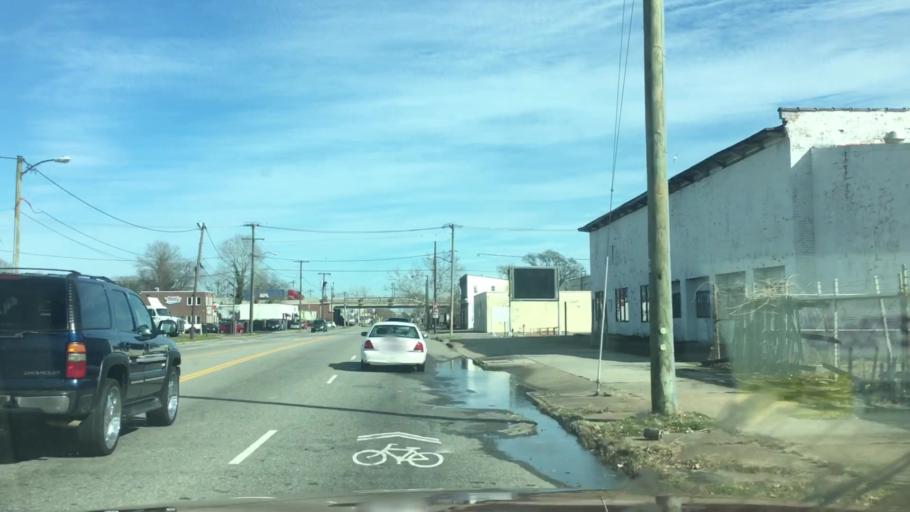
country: US
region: Virginia
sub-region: City of Portsmouth
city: Portsmouth
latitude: 36.8346
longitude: -76.3303
